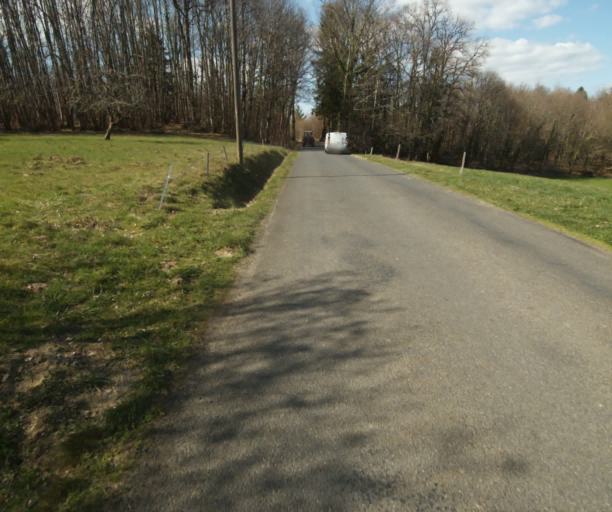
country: FR
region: Limousin
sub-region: Departement de la Correze
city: Saint-Mexant
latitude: 45.2889
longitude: 1.6561
